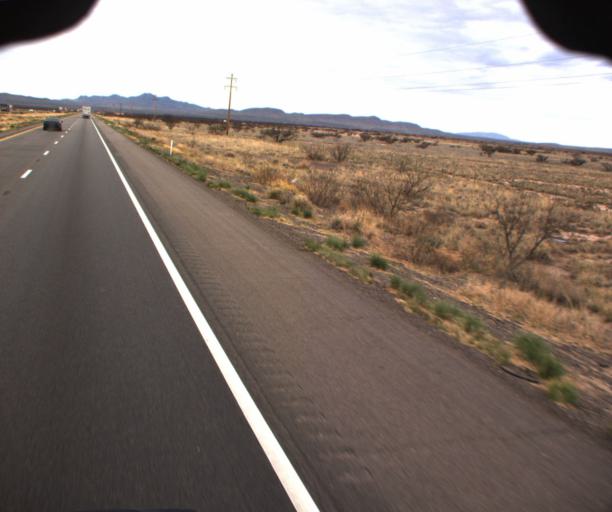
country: US
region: Arizona
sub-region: Cochise County
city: Willcox
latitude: 32.2065
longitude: -109.8993
